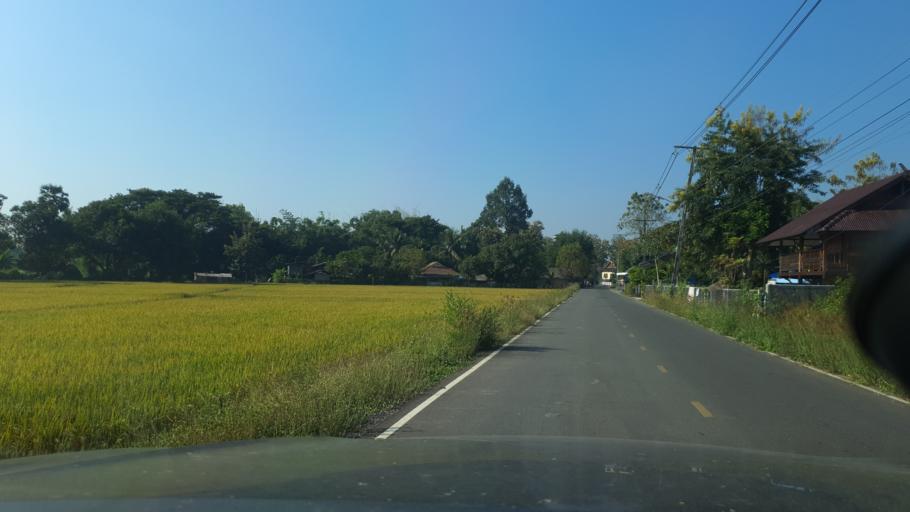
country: TH
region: Chiang Mai
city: San Kamphaeng
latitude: 18.7527
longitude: 99.1496
